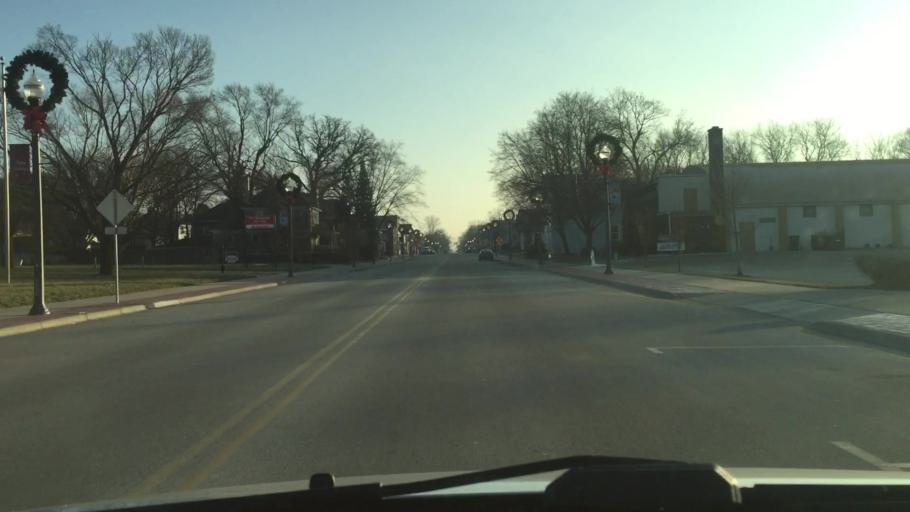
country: US
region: Wisconsin
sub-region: Waukesha County
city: Dousman
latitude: 43.0174
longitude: -88.4728
